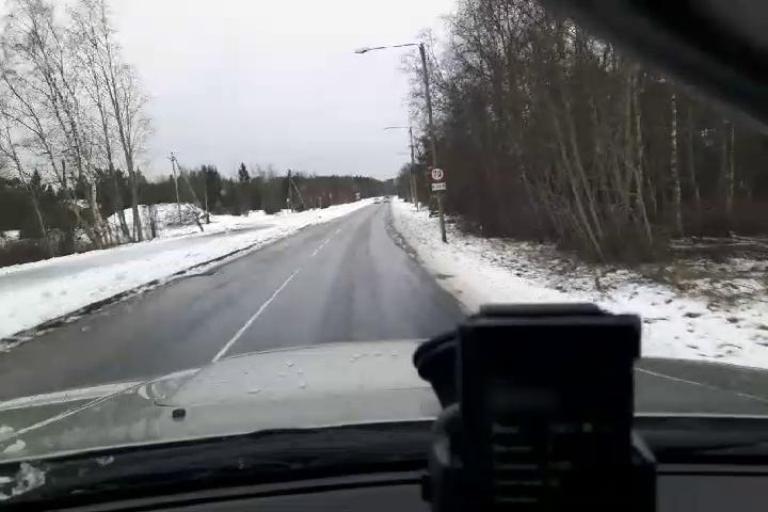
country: EE
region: Harju
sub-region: Harku vald
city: Tabasalu
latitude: 59.4352
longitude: 24.4965
